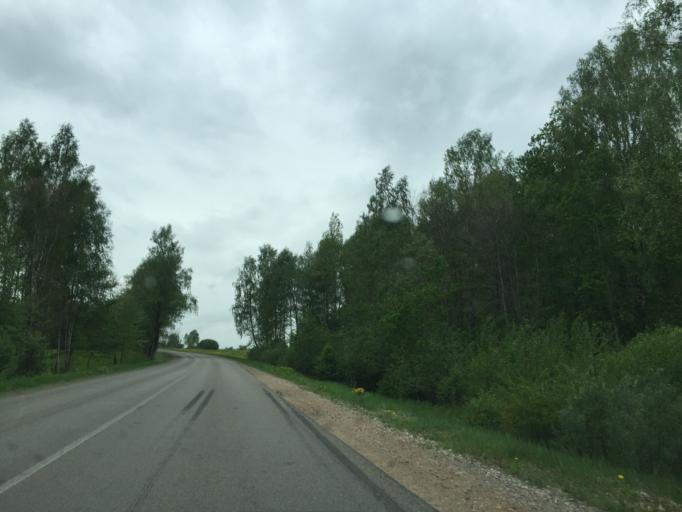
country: LV
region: Lielvarde
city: Lielvarde
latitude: 56.8004
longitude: 24.8518
